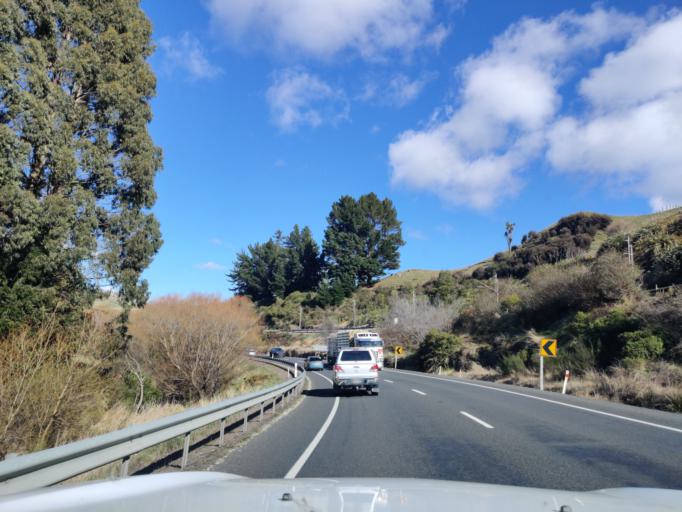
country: NZ
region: Manawatu-Wanganui
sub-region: Ruapehu District
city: Waiouru
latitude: -39.5639
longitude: 175.6977
